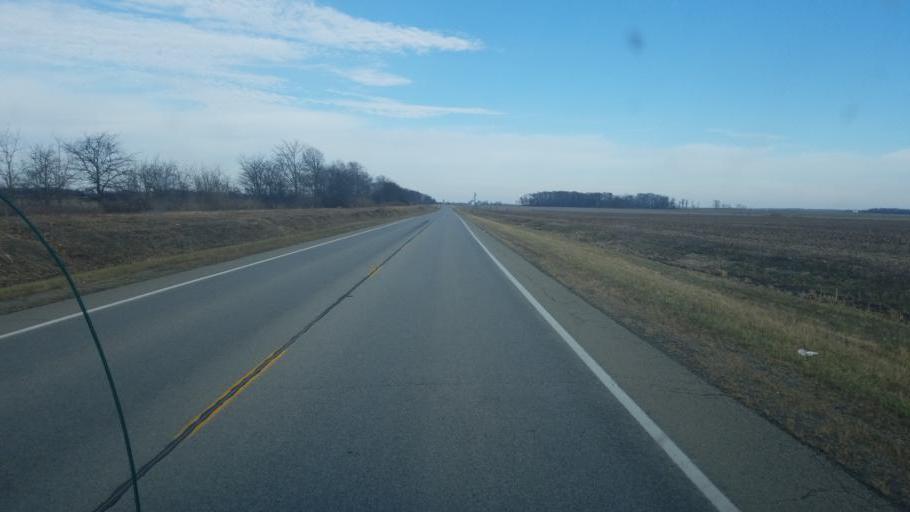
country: US
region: Illinois
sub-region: White County
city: Carmi
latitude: 38.1279
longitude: -88.1027
